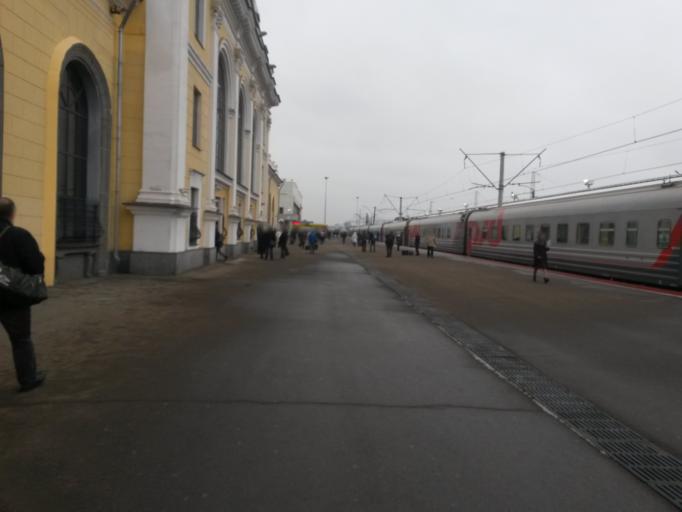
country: RU
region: Jaroslavl
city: Yaroslavl
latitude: 57.6258
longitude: 39.8348
